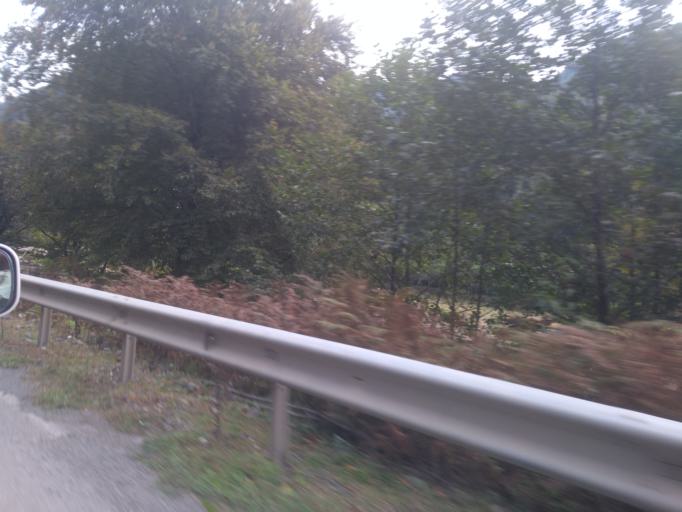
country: TR
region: Artvin
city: Camili
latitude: 41.5664
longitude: 41.8378
